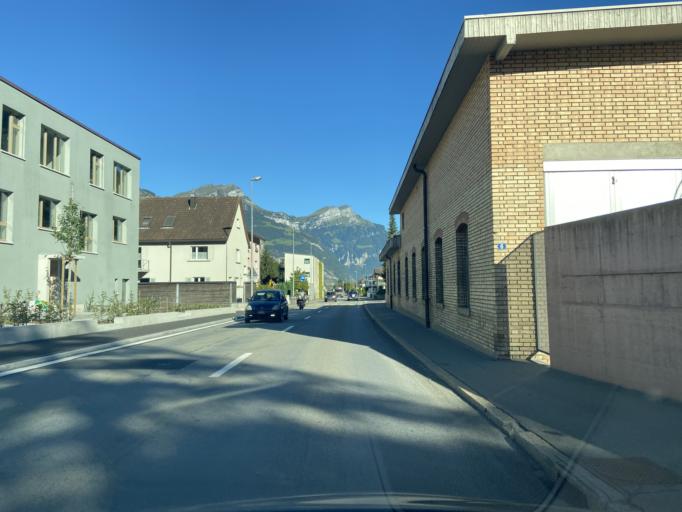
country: CH
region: Uri
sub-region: Uri
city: Altdorf
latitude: 46.8844
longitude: 8.6368
